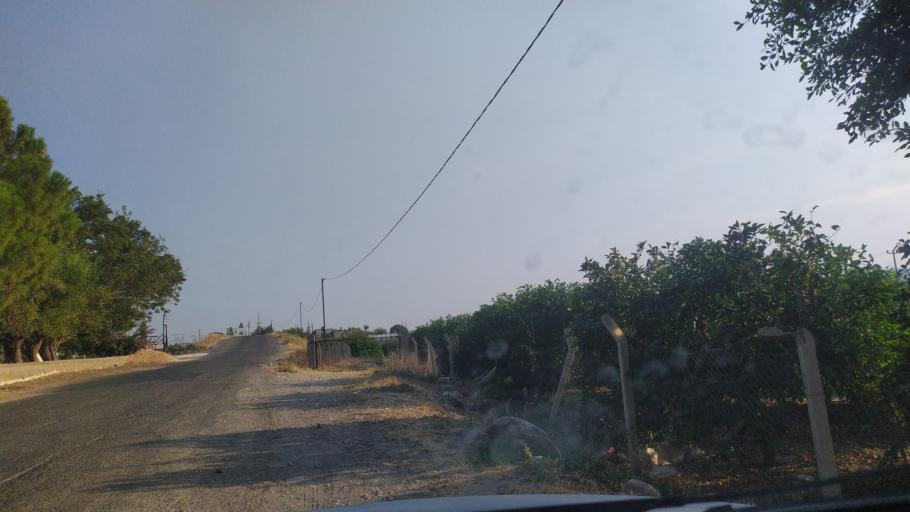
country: TR
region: Mersin
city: Silifke
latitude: 36.4004
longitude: 33.9266
